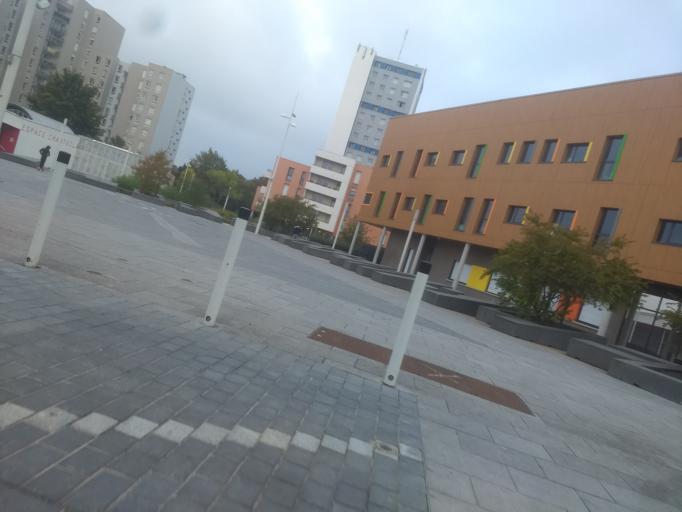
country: FR
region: Nord-Pas-de-Calais
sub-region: Departement du Pas-de-Calais
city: Saint-Nicolas
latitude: 50.3049
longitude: 2.7917
